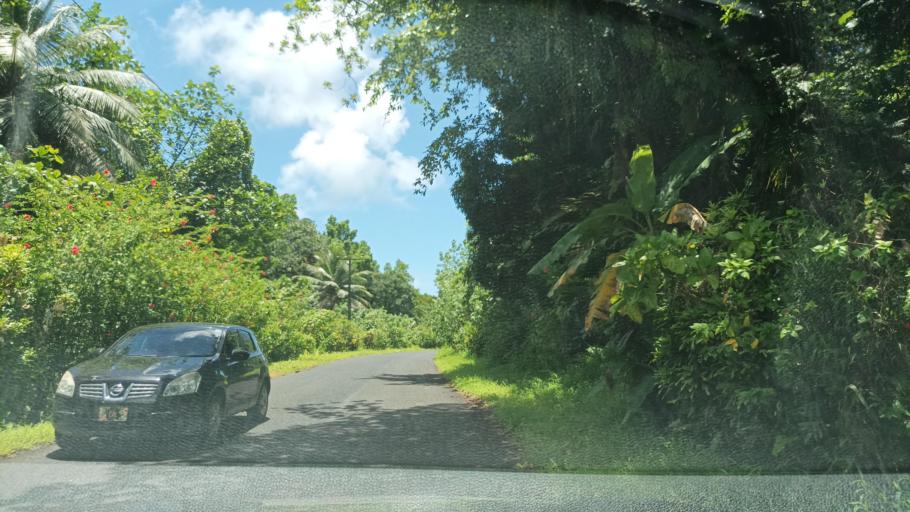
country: FM
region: Pohnpei
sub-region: Madolenihm Municipality
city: Madolenihm Municipality Government
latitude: 6.8658
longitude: 158.2899
